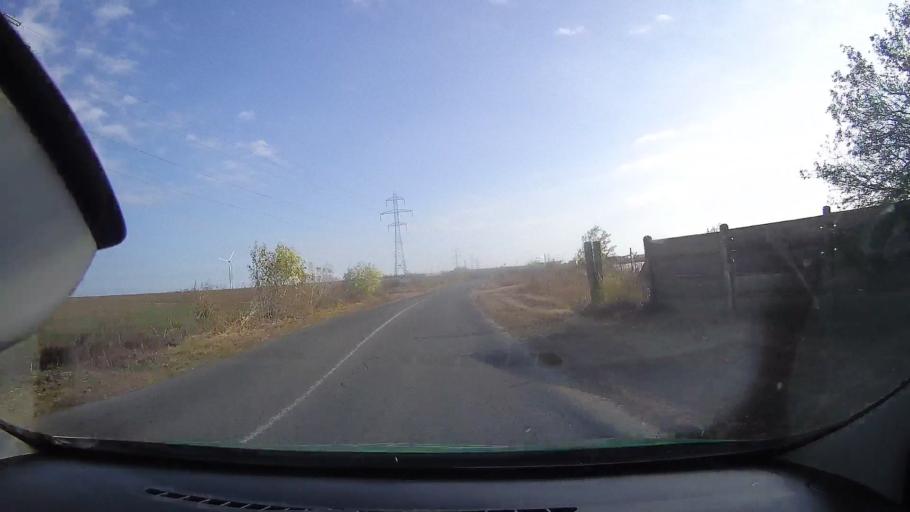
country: RO
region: Constanta
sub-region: Comuna Corbu
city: Corbu
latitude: 44.3663
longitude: 28.6718
